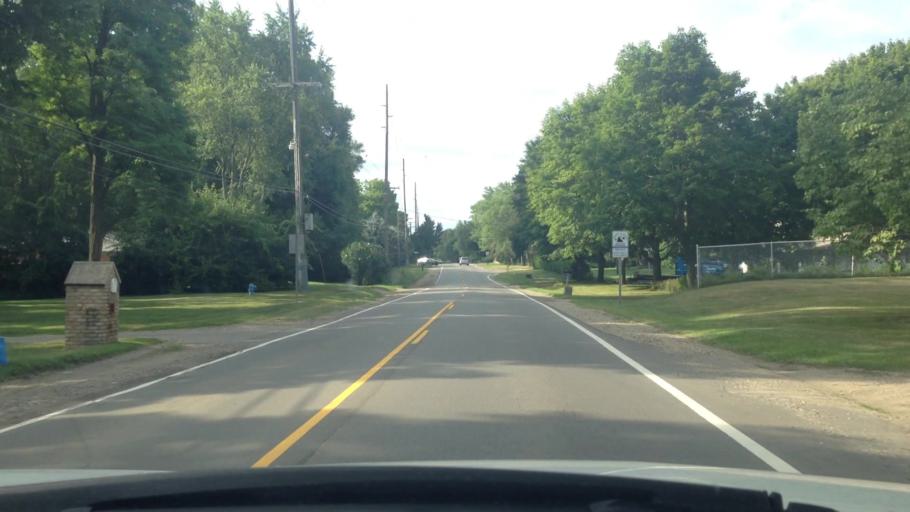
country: US
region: Michigan
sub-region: Oakland County
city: Waterford
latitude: 42.7044
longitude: -83.3488
